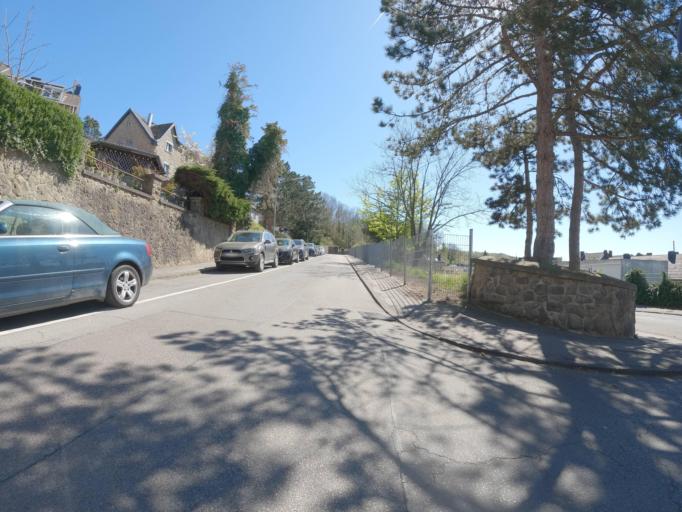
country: DE
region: North Rhine-Westphalia
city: Stolberg
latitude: 50.7709
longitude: 6.2331
